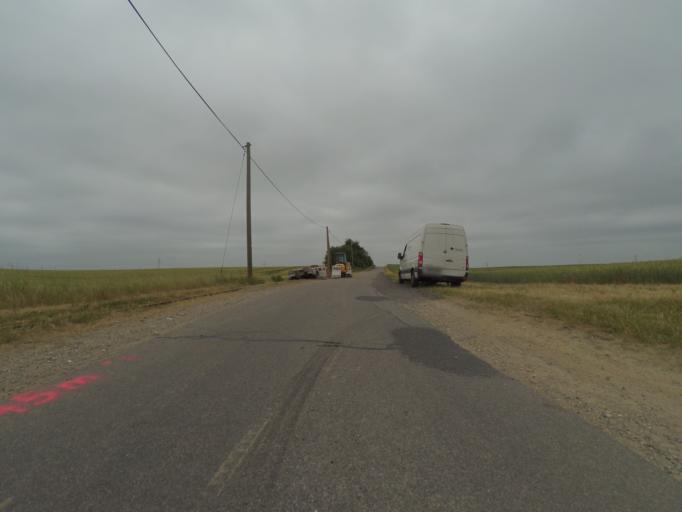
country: DE
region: Mecklenburg-Vorpommern
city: Gaegelow
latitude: 53.7012
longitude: 11.8696
